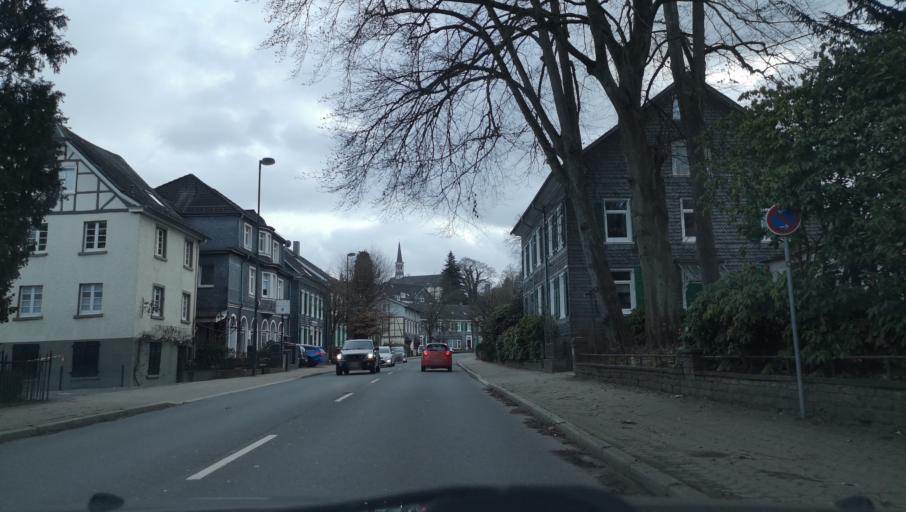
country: DE
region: North Rhine-Westphalia
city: Huckeswagen
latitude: 51.1504
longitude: 7.3387
